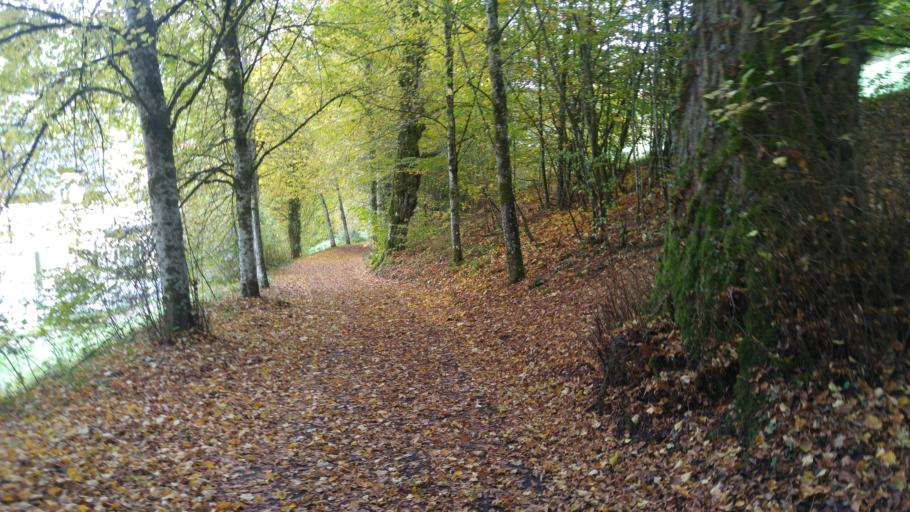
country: DE
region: Baden-Wuerttemberg
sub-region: Karlsruhe Region
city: Bad Teinach-Zavelstein
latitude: 48.6875
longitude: 8.6837
